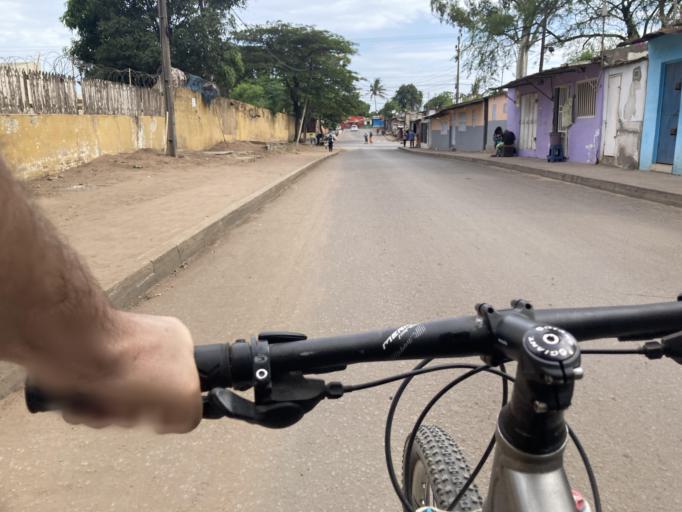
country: MZ
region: Maputo City
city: Maputo
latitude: -25.9315
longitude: 32.5846
